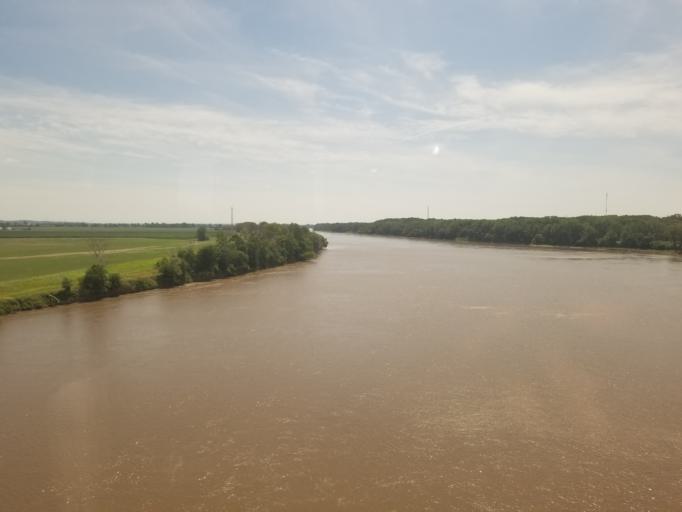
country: US
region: Missouri
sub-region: Jackson County
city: Buckner
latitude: 39.1806
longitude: -94.1788
